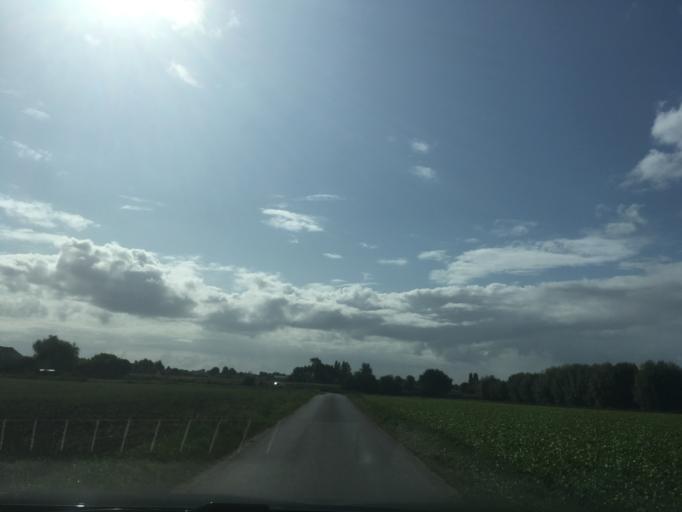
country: BE
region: Flanders
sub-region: Provincie West-Vlaanderen
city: Staden
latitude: 51.0002
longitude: 3.0269
